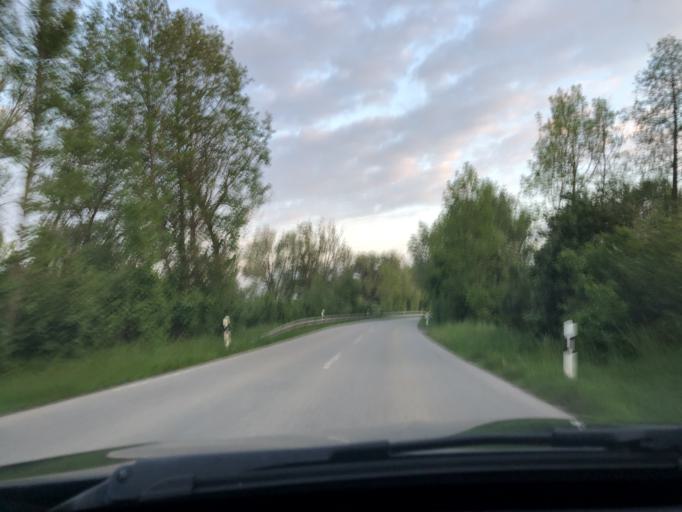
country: DE
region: Bavaria
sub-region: Upper Bavaria
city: Wolfersdorf
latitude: 48.4549
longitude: 11.7081
